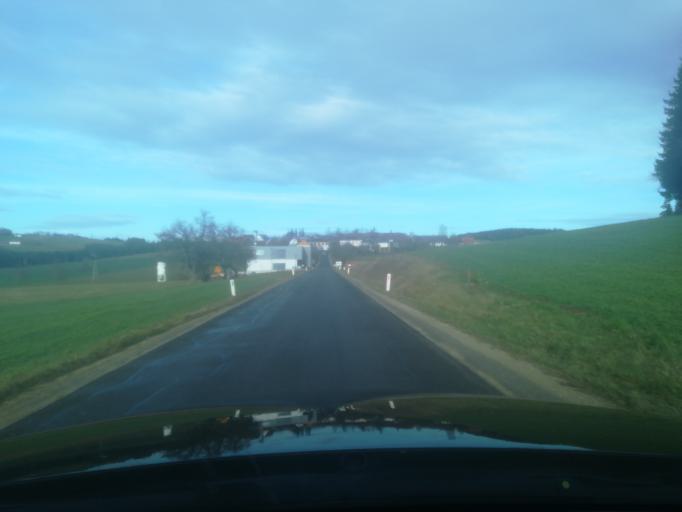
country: AT
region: Upper Austria
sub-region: Politischer Bezirk Perg
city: Perg
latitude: 48.3650
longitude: 14.6319
